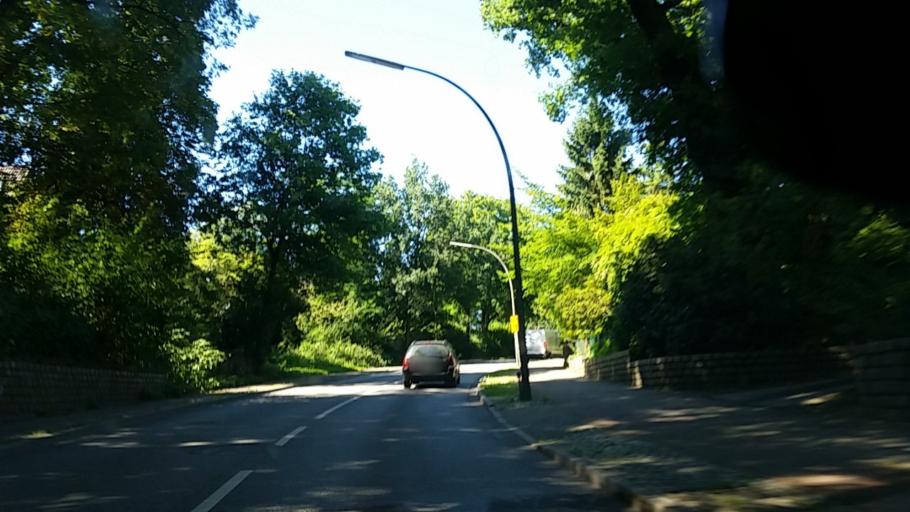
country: DE
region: Hamburg
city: Harburg
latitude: 53.4548
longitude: 9.9545
